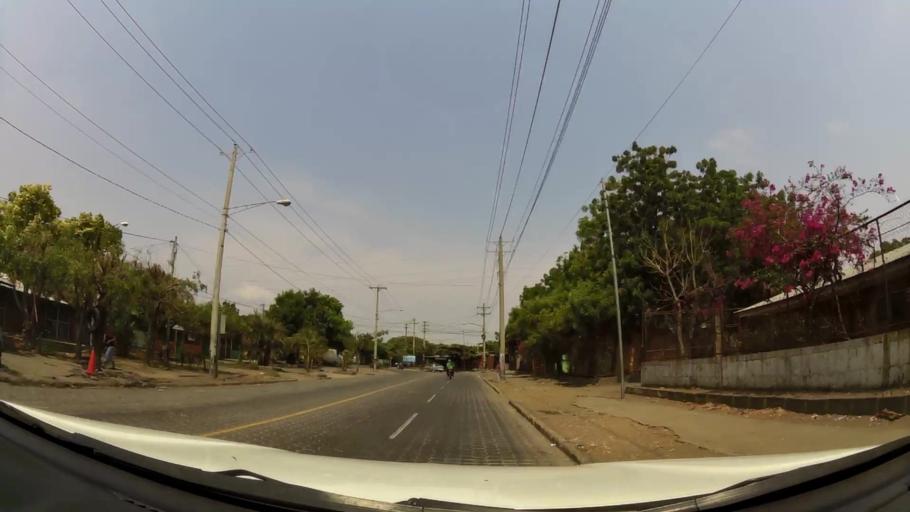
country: NI
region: Managua
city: Ciudad Sandino
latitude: 12.1583
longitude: -86.3037
